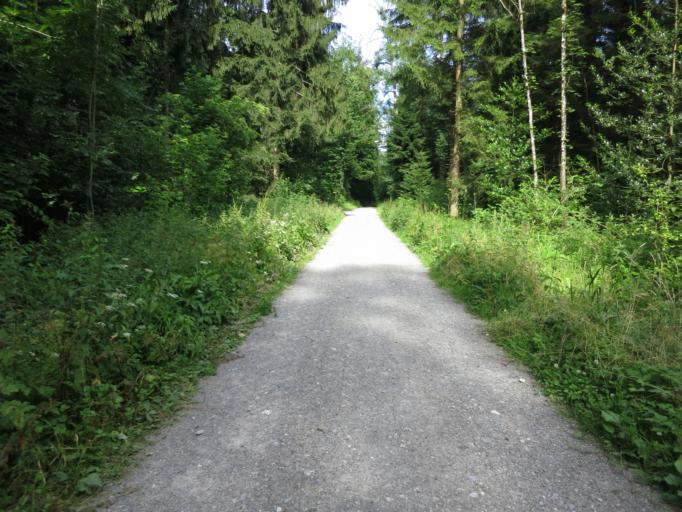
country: CH
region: Zurich
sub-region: Bezirk Hinwil
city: Rueti / Westlicher Dorfteil
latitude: 47.2565
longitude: 8.8297
